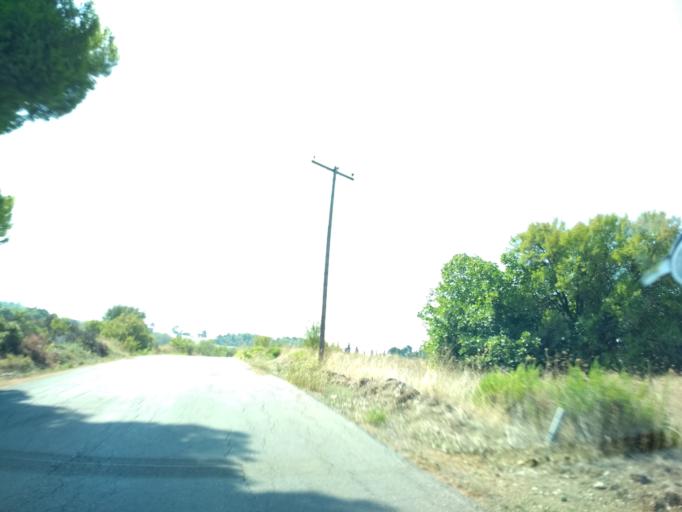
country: GR
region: Central Greece
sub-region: Nomos Evvoias
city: Roviai
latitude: 38.8216
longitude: 23.2664
